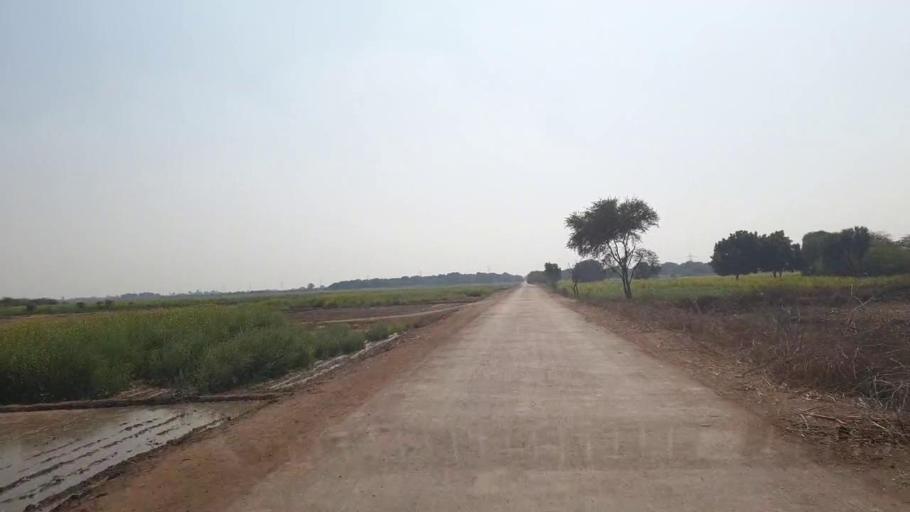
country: PK
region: Sindh
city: Chambar
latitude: 25.3949
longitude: 68.8959
